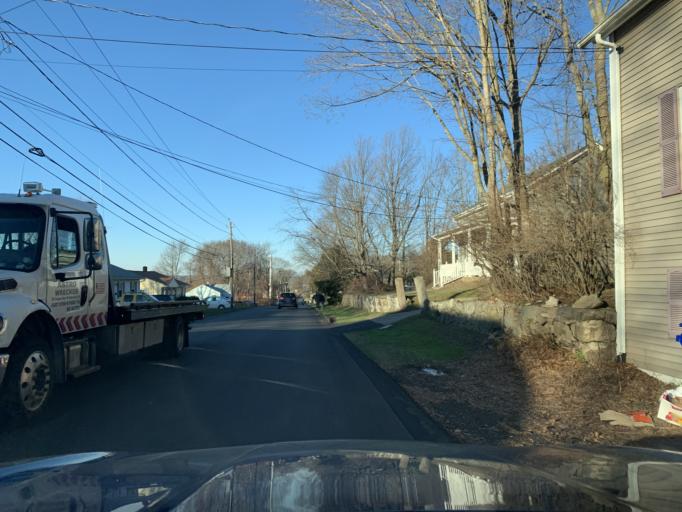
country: US
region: Rhode Island
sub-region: Kent County
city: West Warwick
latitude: 41.6854
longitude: -71.5201
